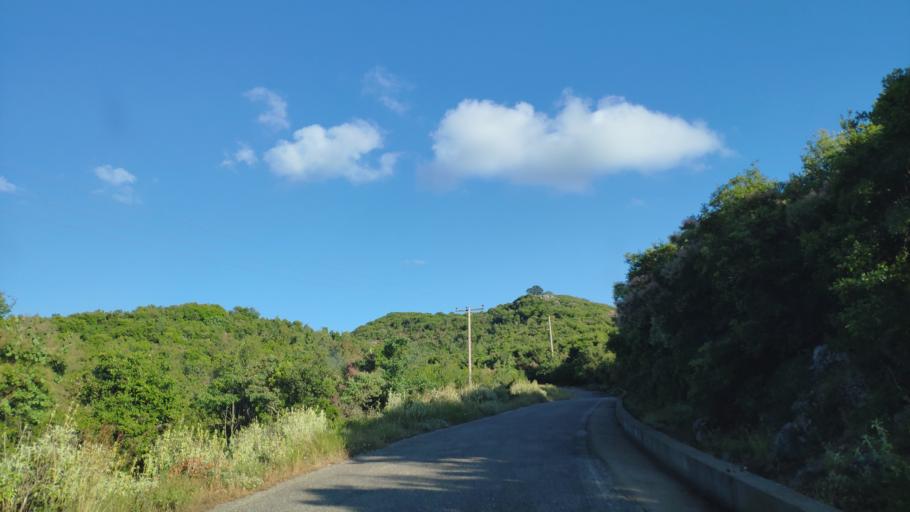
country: GR
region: West Greece
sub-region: Nomos Aitolias kai Akarnanias
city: Fitiai
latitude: 38.6597
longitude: 21.1937
